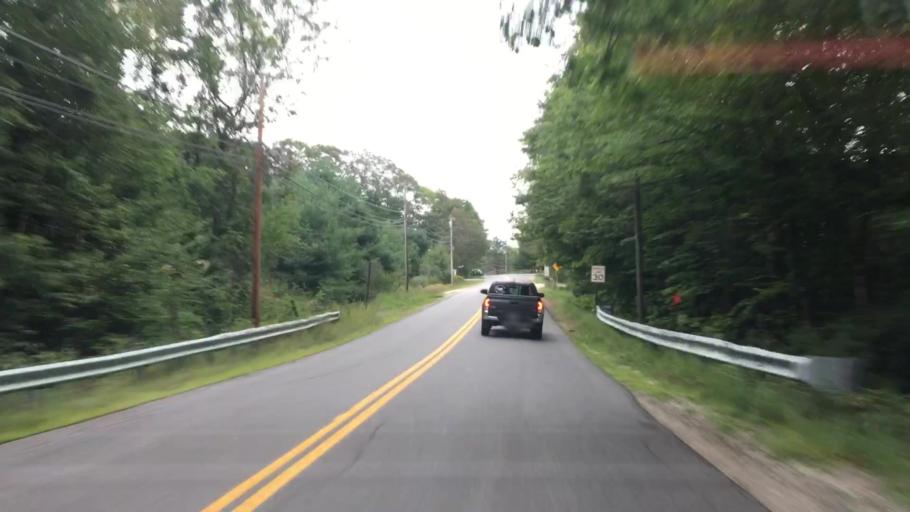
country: US
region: Maine
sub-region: Cumberland County
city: Freeport
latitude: 43.8651
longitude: -70.1168
